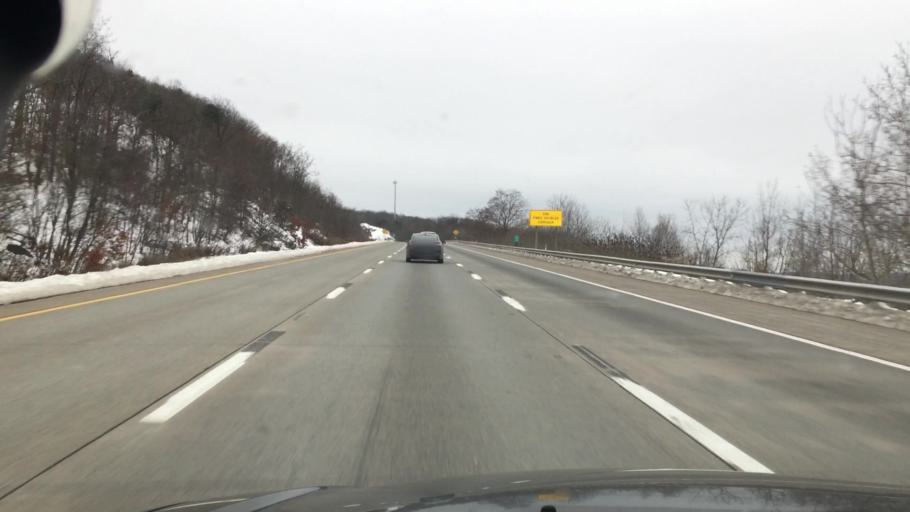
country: US
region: Pennsylvania
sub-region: Luzerne County
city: Nanticoke
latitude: 41.1758
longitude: -75.9496
